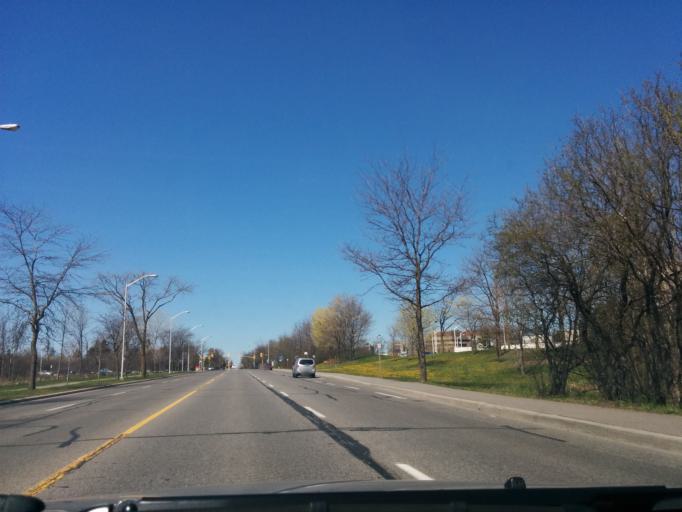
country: CA
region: Ontario
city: Ottawa
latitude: 45.3997
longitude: -75.6441
